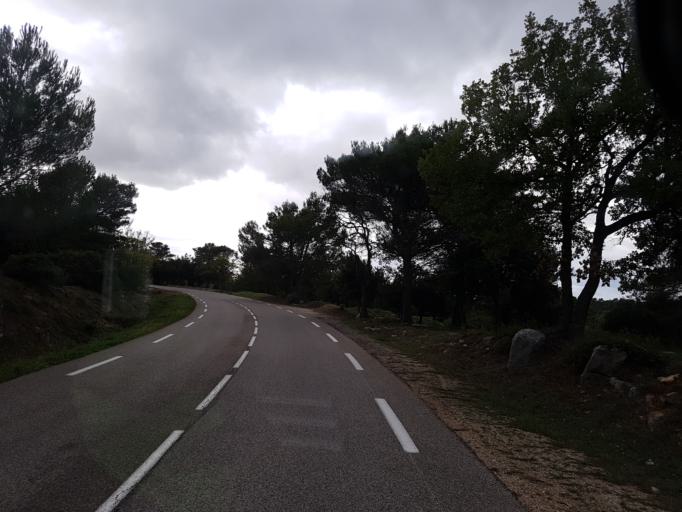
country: FR
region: Provence-Alpes-Cote d'Azur
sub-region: Departement des Bouches-du-Rhone
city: Cuges-les-Pins
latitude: 43.2635
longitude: 5.7486
